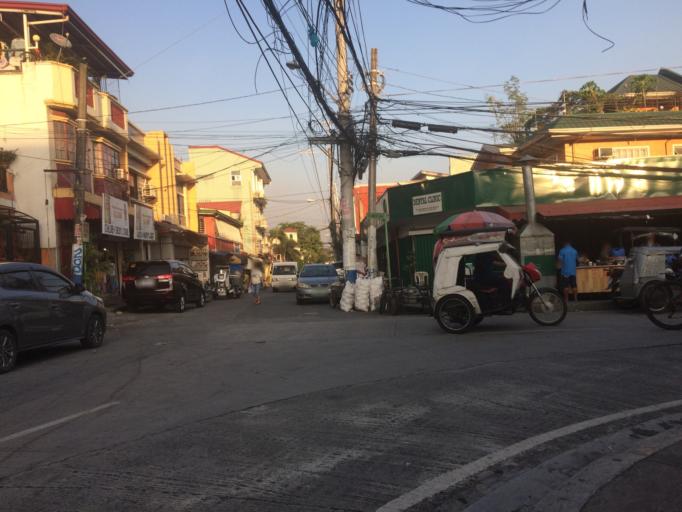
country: PH
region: Calabarzon
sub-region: Province of Rizal
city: Cainta
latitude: 14.5900
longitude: 121.1042
